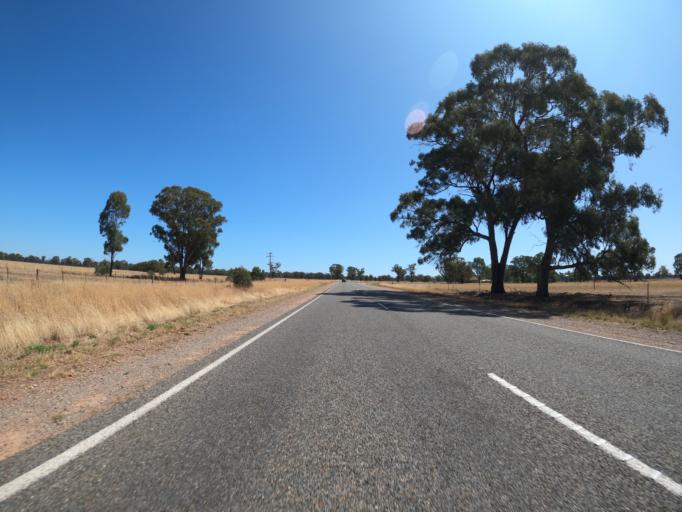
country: AU
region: New South Wales
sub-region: Corowa Shire
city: Corowa
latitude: -36.0760
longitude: 146.3467
